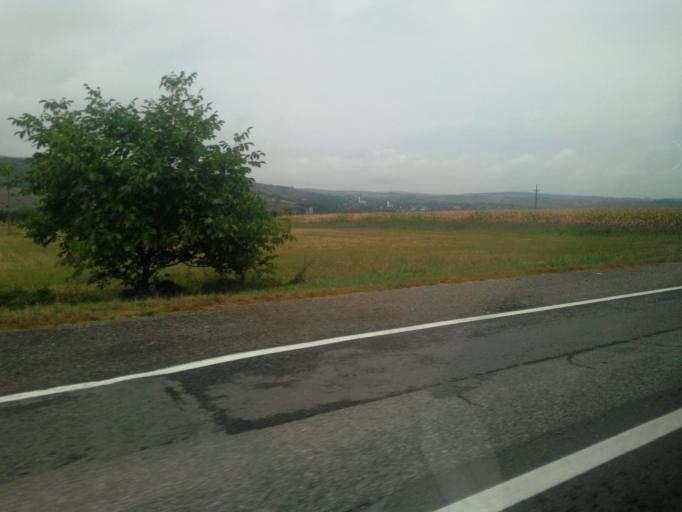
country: RO
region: Cluj
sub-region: Comuna Mihai Viteazu
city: Mihai Viteazu
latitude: 46.5272
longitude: 23.7044
